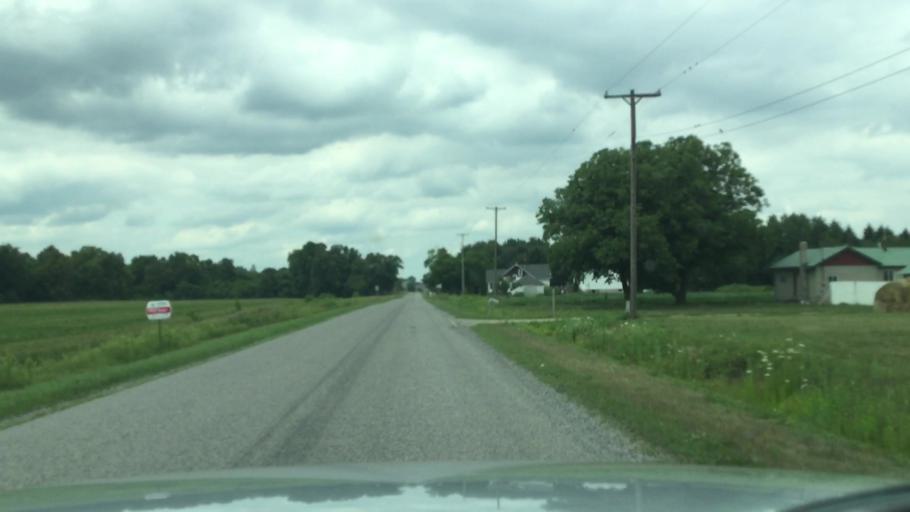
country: US
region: Michigan
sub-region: Saginaw County
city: Burt
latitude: 43.2586
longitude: -83.8750
